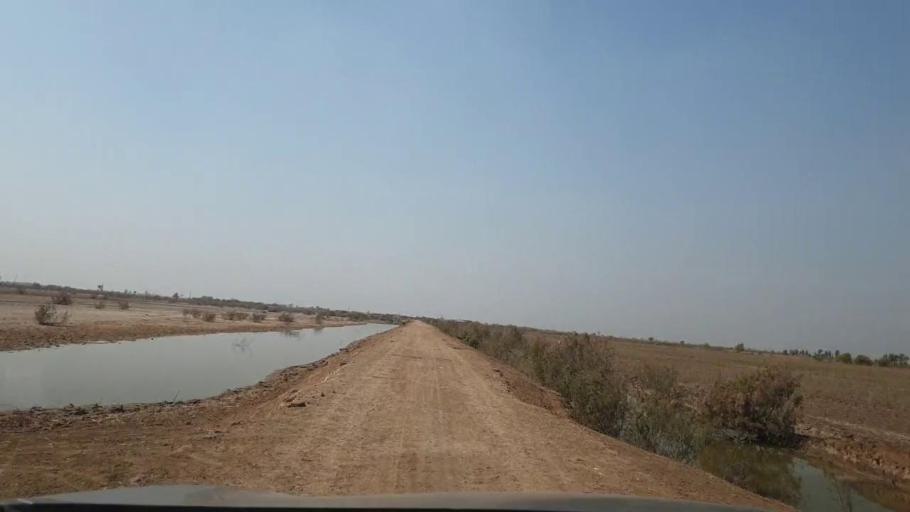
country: PK
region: Sindh
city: Berani
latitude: 25.6629
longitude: 68.8746
